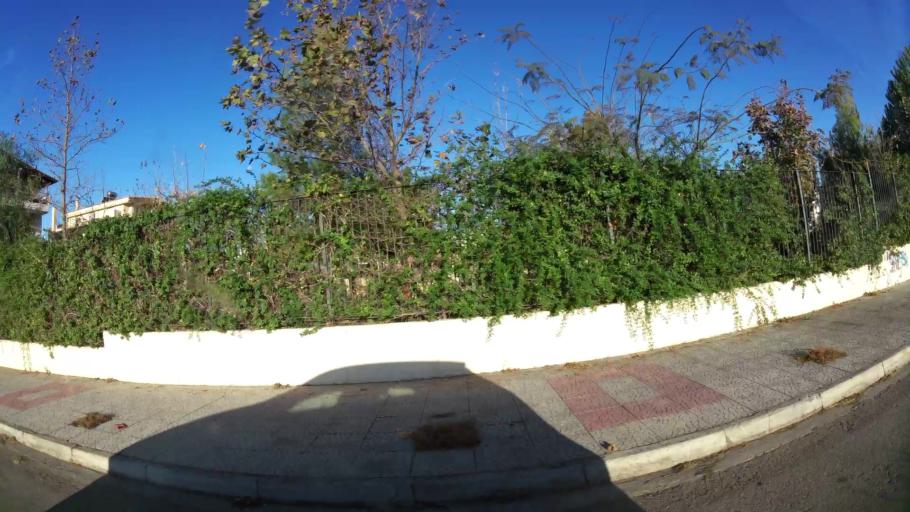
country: GR
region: Attica
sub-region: Nomarchia Anatolikis Attikis
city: Gerakas
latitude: 38.0289
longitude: 23.8470
